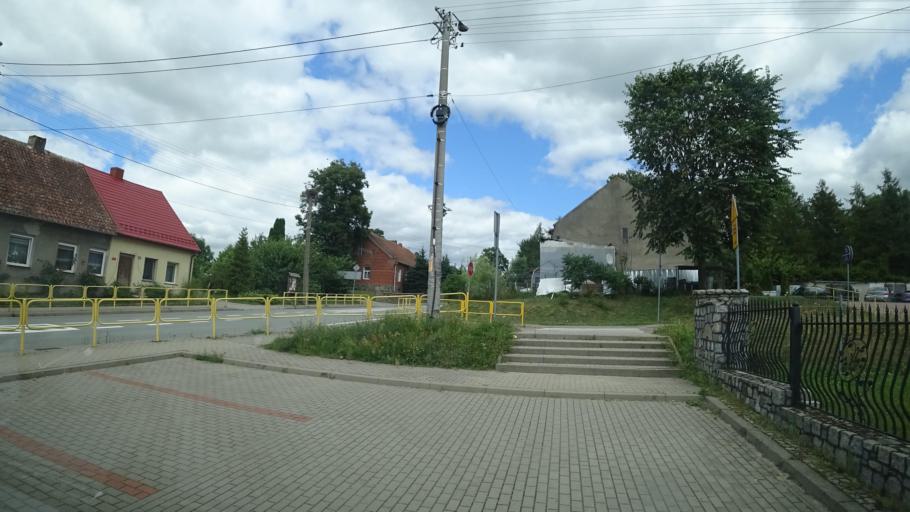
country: PL
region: Warmian-Masurian Voivodeship
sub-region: Powiat goldapski
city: Goldap
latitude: 54.2256
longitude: 22.2400
